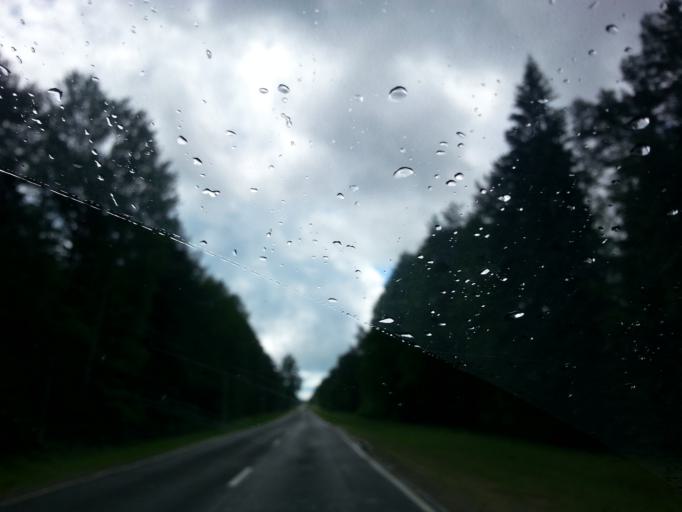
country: BY
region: Minsk
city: Narach
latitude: 54.8656
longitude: 26.6733
